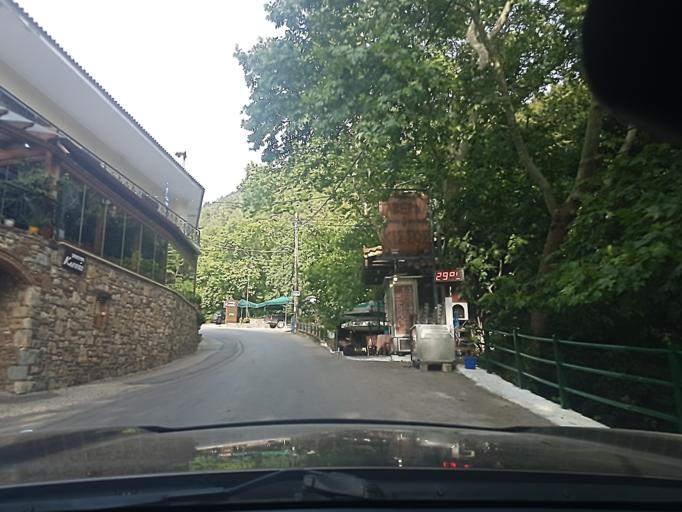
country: GR
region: Central Greece
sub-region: Nomos Evvoias
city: Yimnon
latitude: 38.5827
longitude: 23.8392
